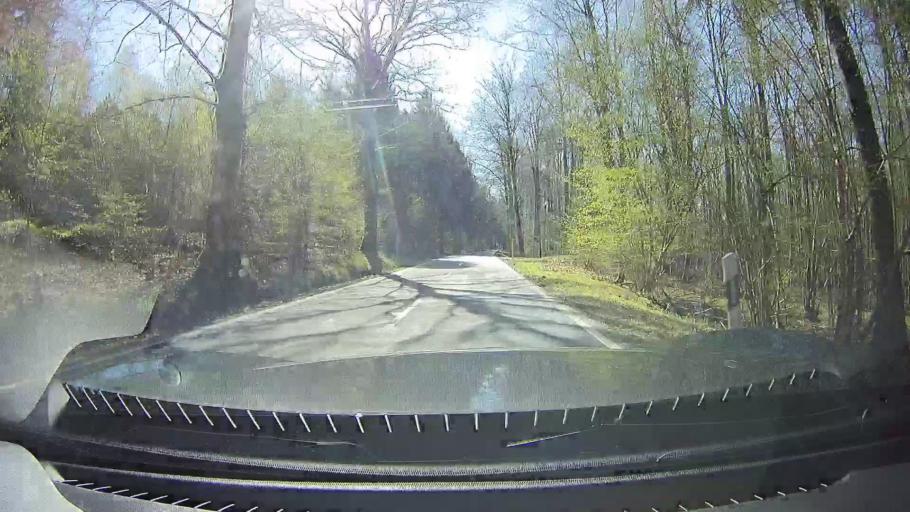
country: DE
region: Baden-Wuerttemberg
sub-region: Karlsruhe Region
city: Eberbach
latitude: 49.4254
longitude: 8.9785
